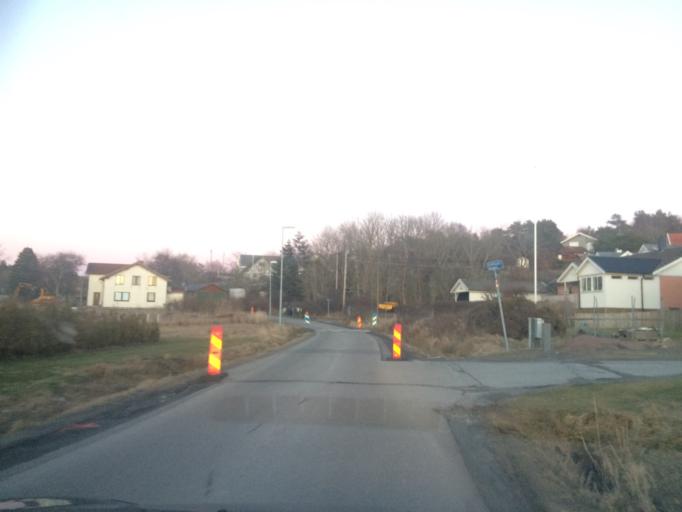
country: SE
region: Vaestra Goetaland
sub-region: Goteborg
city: Torslanda
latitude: 57.7799
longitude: 11.8300
